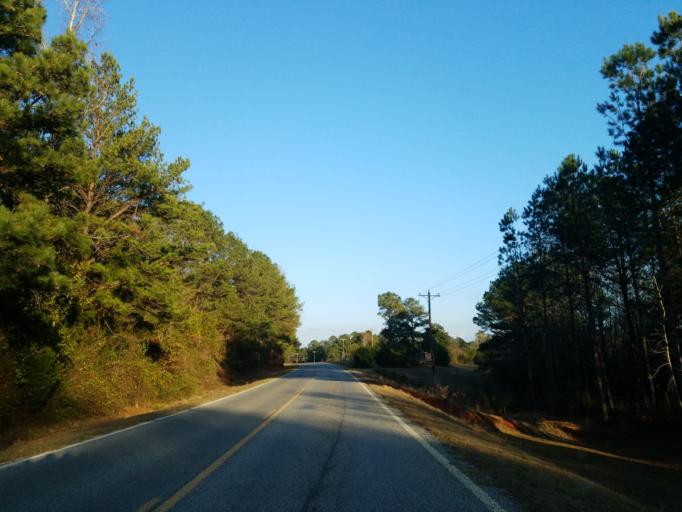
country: US
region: Mississippi
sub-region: Clarke County
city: Stonewall
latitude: 32.1675
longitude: -88.8496
